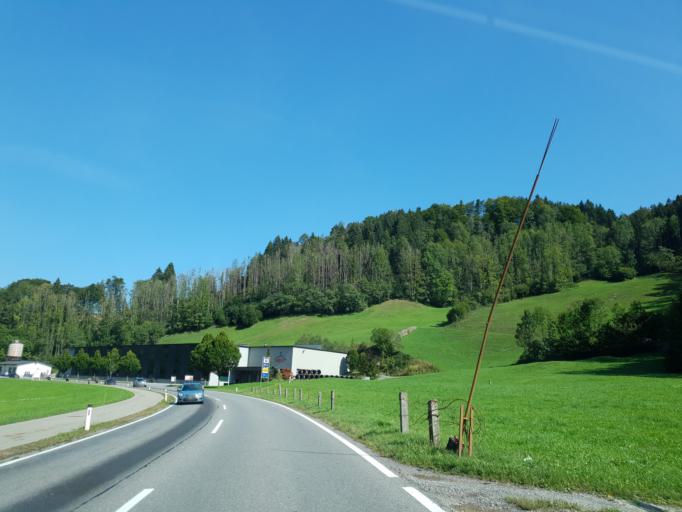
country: AT
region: Vorarlberg
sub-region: Politischer Bezirk Bregenz
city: Andelsbuch
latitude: 47.3941
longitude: 9.8551
